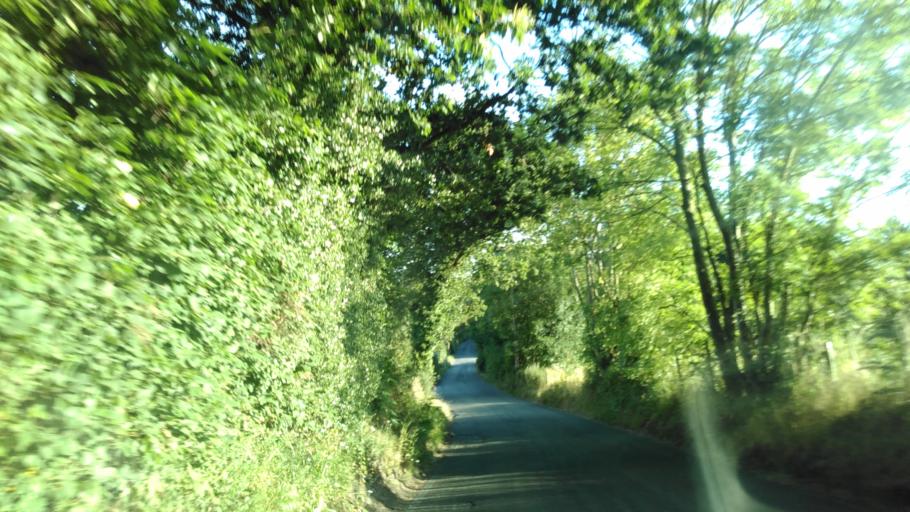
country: GB
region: England
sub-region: Kent
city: Dunkirk
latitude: 51.2828
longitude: 1.0067
